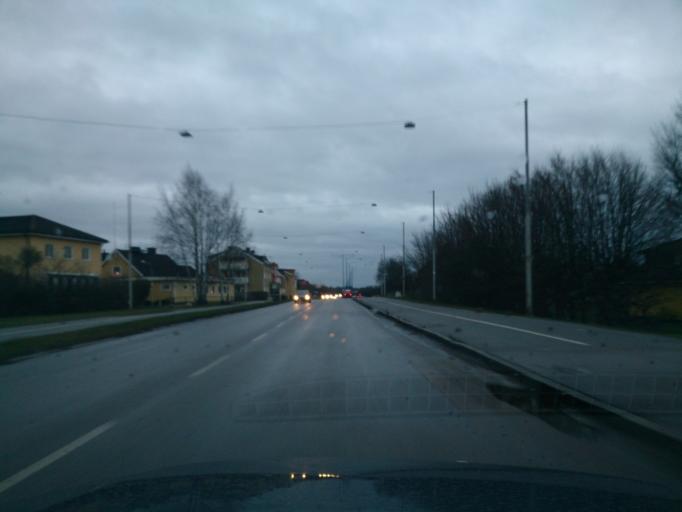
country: SE
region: OEstergoetland
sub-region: Norrkopings Kommun
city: Norrkoping
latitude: 58.6021
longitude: 16.1442
